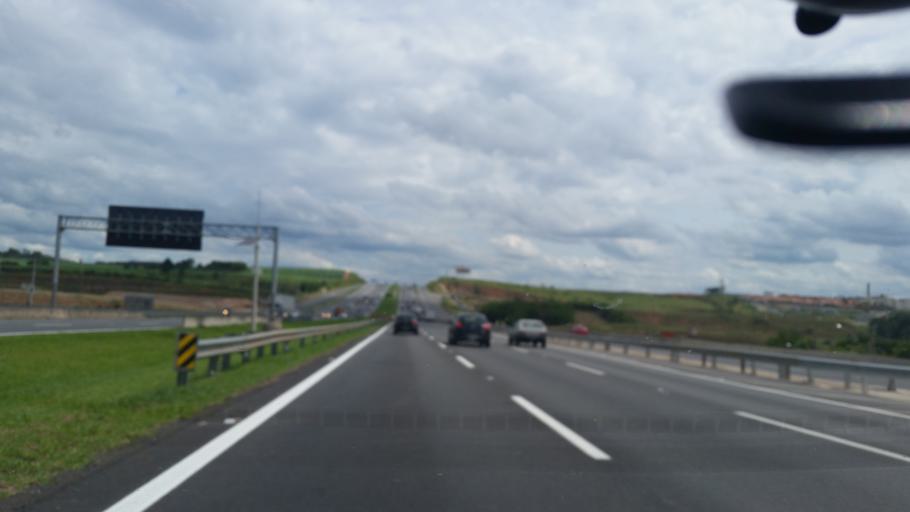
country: BR
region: Sao Paulo
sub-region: Campinas
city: Campinas
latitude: -22.8655
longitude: -47.0208
